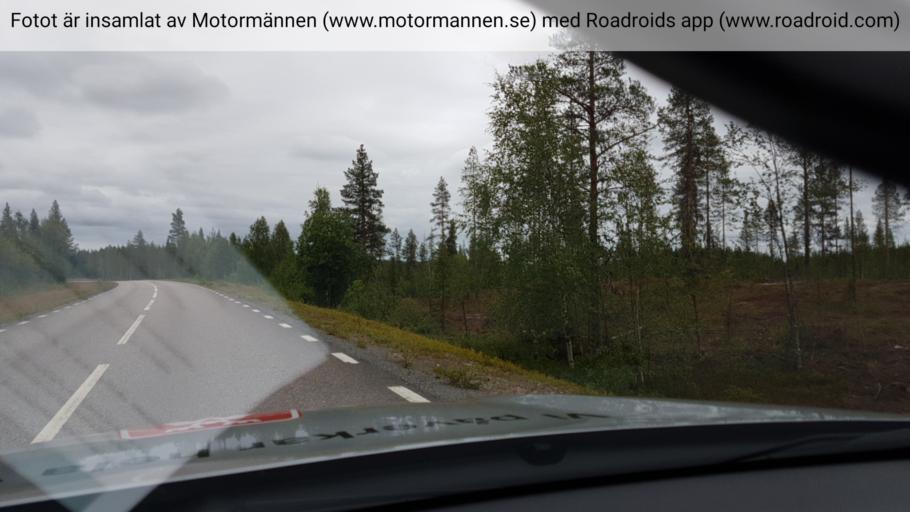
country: SE
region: Norrbotten
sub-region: Overkalix Kommun
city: OEverkalix
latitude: 67.0093
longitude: 21.8852
